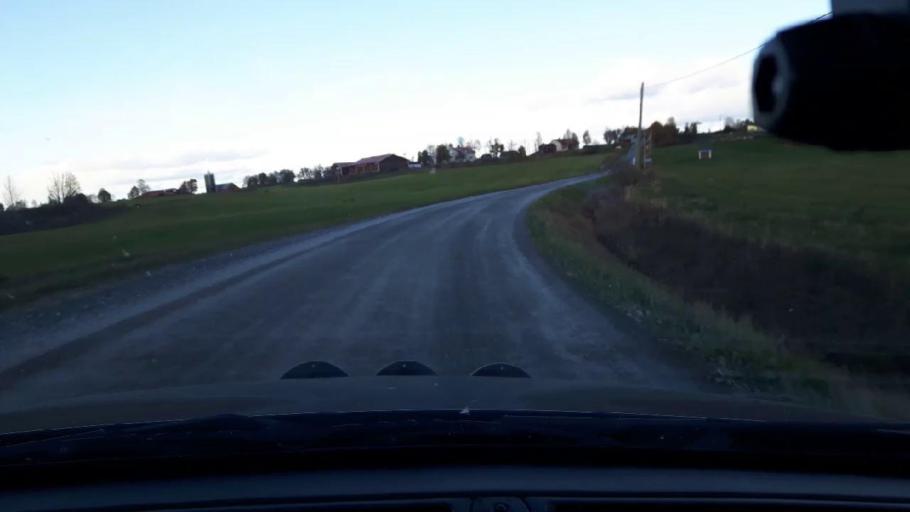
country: SE
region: Jaemtland
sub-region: Krokoms Kommun
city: Krokom
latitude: 63.0769
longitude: 14.2719
